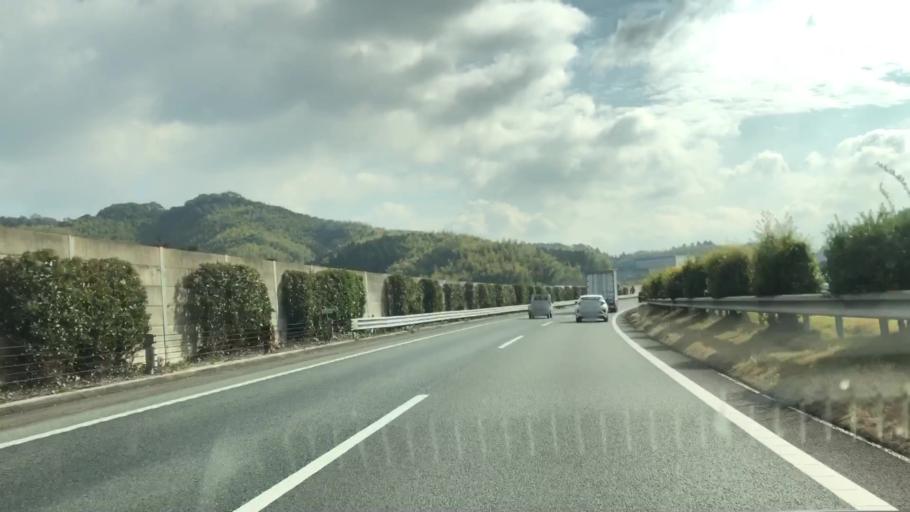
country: JP
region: Fukuoka
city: Setakamachi-takayanagi
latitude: 33.0861
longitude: 130.5411
